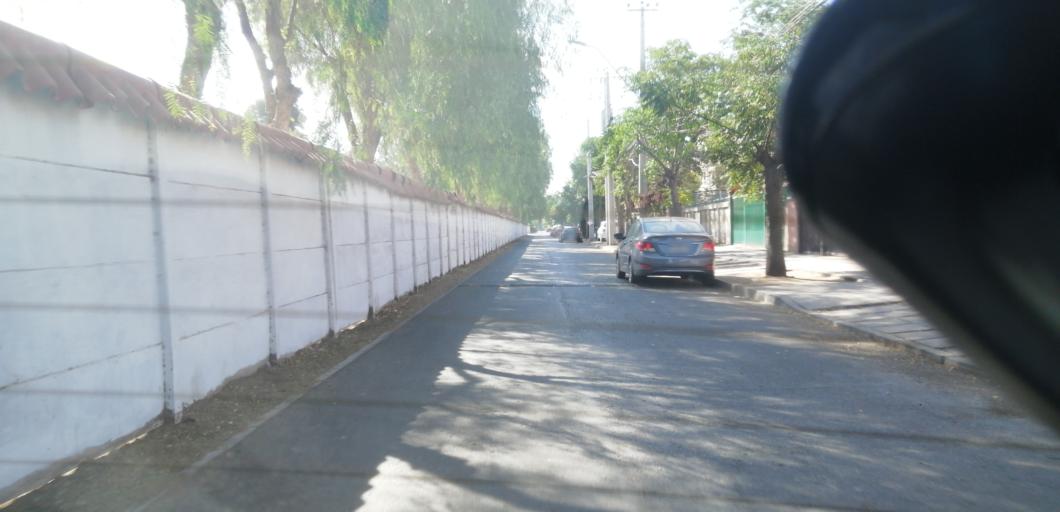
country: CL
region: Santiago Metropolitan
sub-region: Provincia de Santiago
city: Lo Prado
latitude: -33.4629
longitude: -70.7251
